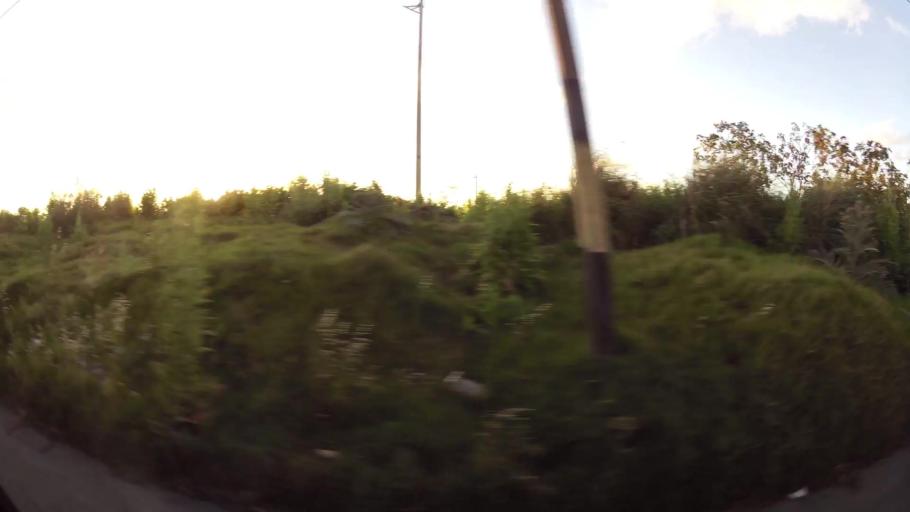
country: UY
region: Canelones
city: Paso de Carrasco
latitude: -34.8794
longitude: -56.1186
